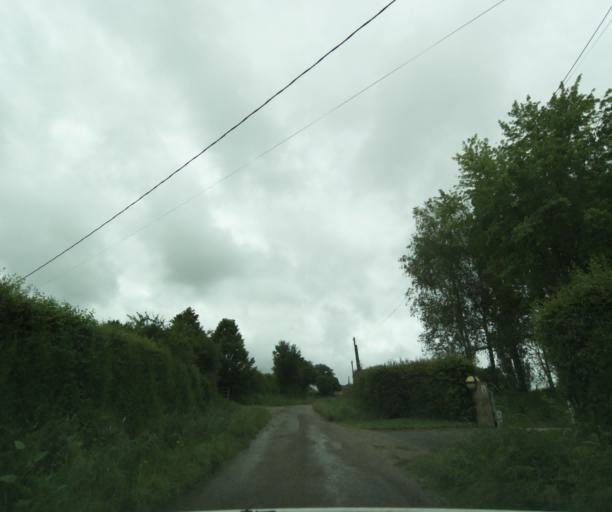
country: FR
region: Bourgogne
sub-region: Departement de Saone-et-Loire
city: Charolles
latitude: 46.4855
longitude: 4.3222
